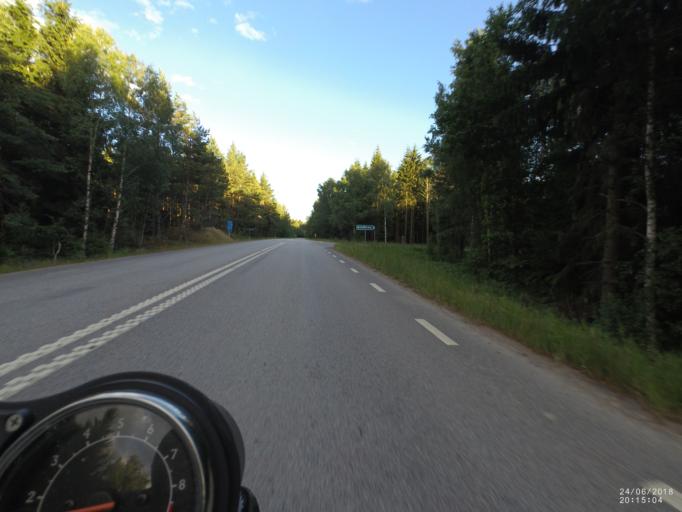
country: SE
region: Soedermanland
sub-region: Nykopings Kommun
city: Nykoping
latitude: 58.7849
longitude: 17.0720
